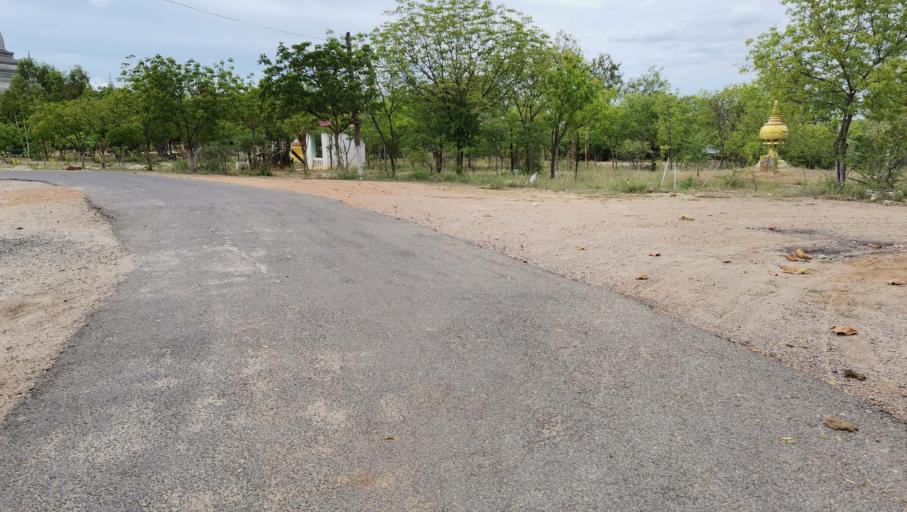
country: MM
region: Mandalay
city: Myingyan
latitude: 21.8248
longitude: 95.3954
